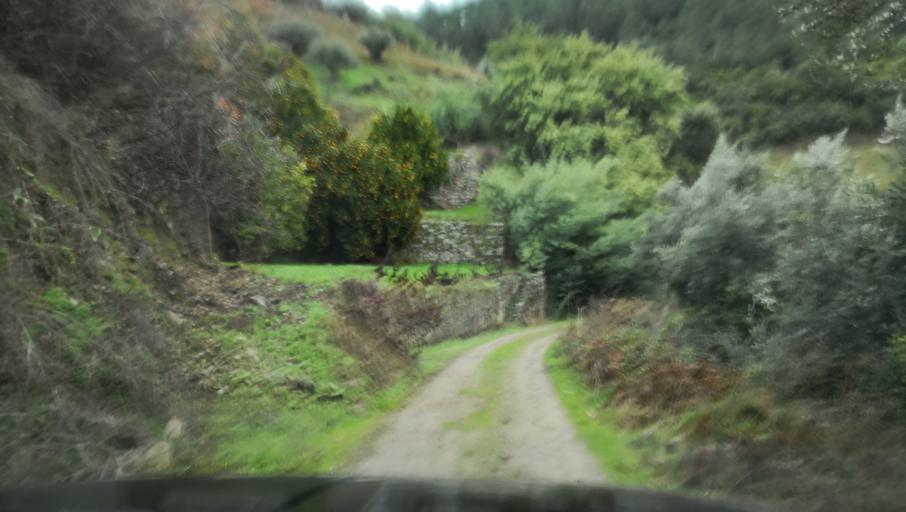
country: PT
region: Vila Real
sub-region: Vila Real
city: Vila Real
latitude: 41.2694
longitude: -7.7365
